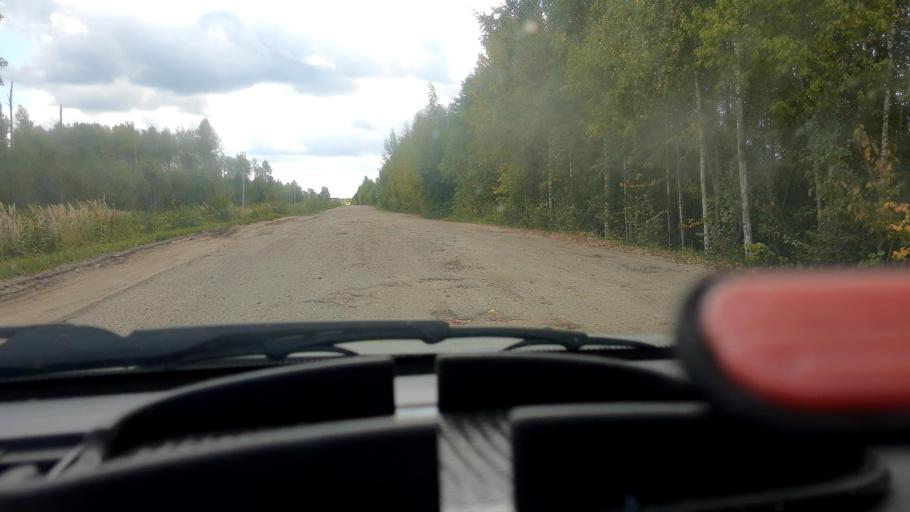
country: RU
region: Mariy-El
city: Kilemary
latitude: 56.8949
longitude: 46.7506
